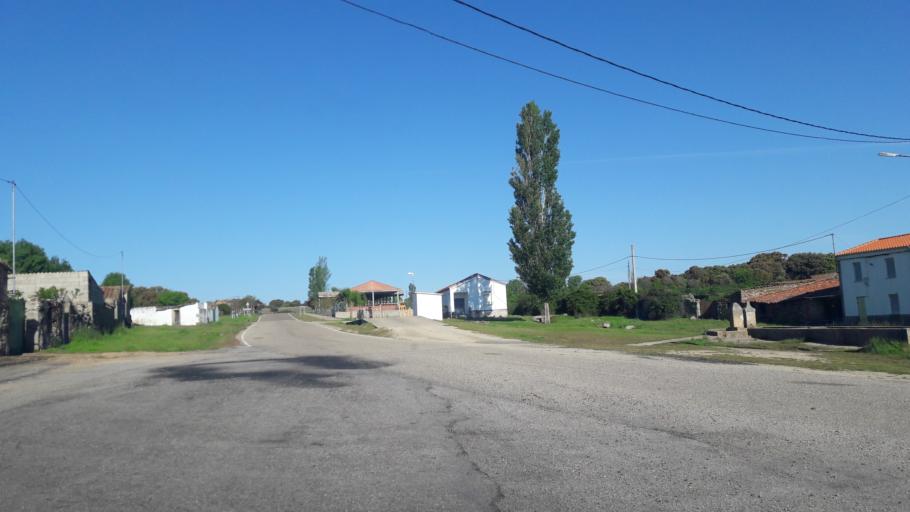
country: ES
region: Castille and Leon
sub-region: Provincia de Salamanca
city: Bogajo
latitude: 40.9070
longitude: -6.5338
